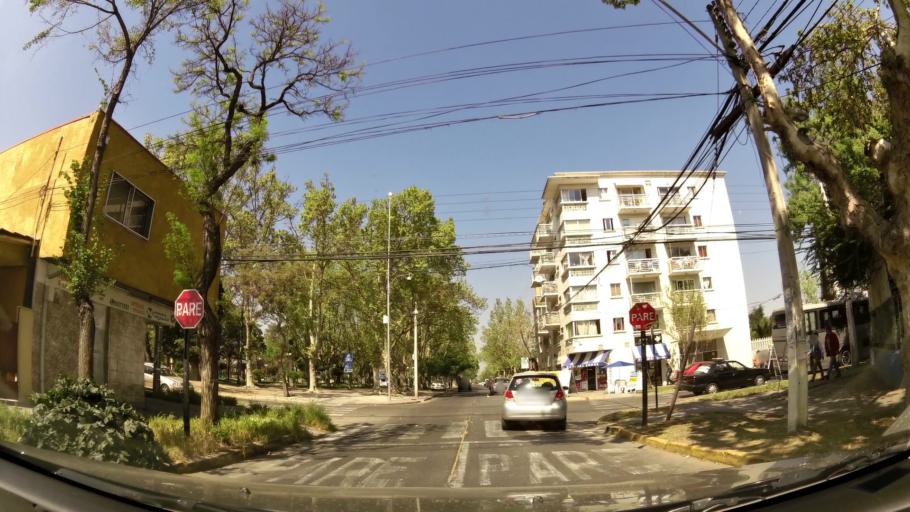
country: CL
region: Santiago Metropolitan
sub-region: Provincia de Maipo
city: San Bernardo
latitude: -33.6024
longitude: -70.7043
